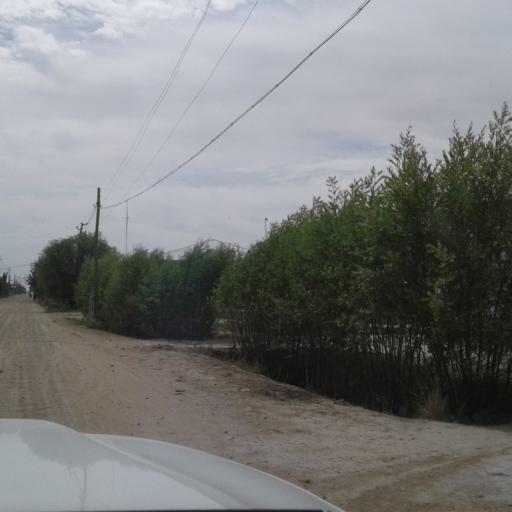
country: TM
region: Dasoguz
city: Tagta
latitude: 41.6019
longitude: 59.8471
